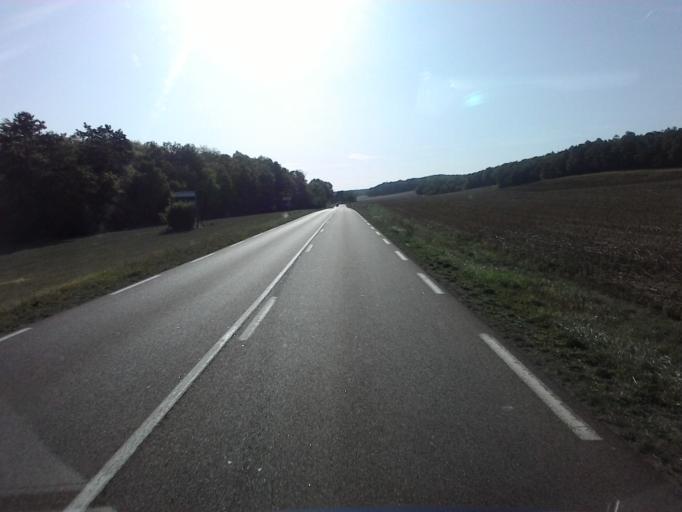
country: FR
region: Champagne-Ardenne
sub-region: Departement de l'Aube
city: Bar-sur-Seine
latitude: 48.1323
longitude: 4.3354
